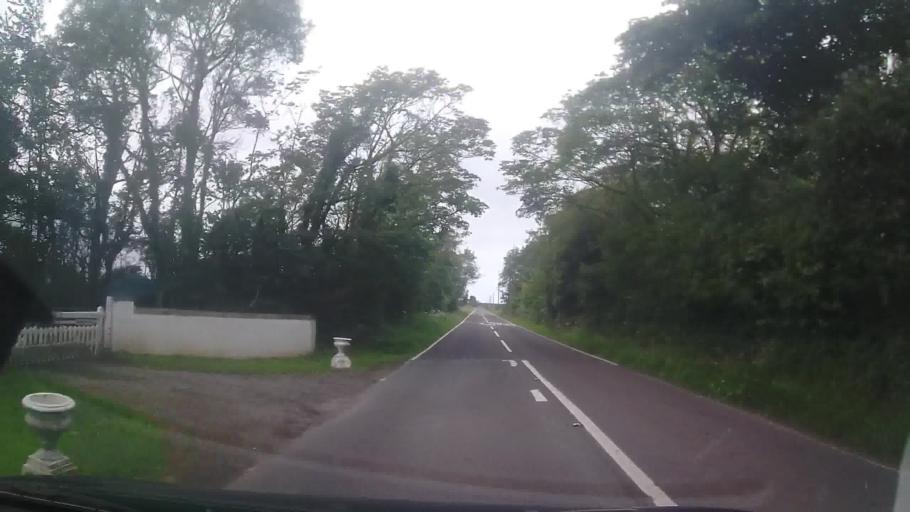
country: GB
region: Wales
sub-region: Gwynedd
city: Caernarfon
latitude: 53.1663
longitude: -4.3355
